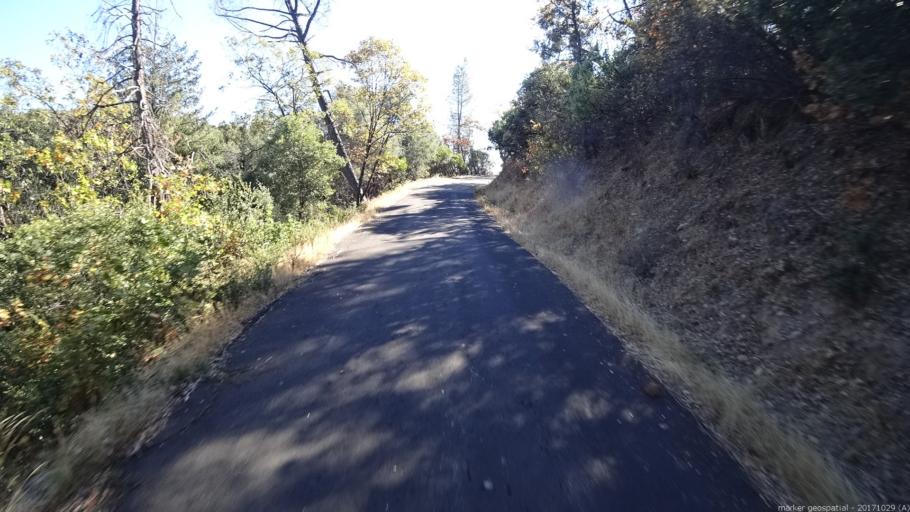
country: US
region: California
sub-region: Shasta County
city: Shasta
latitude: 40.4801
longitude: -122.6743
